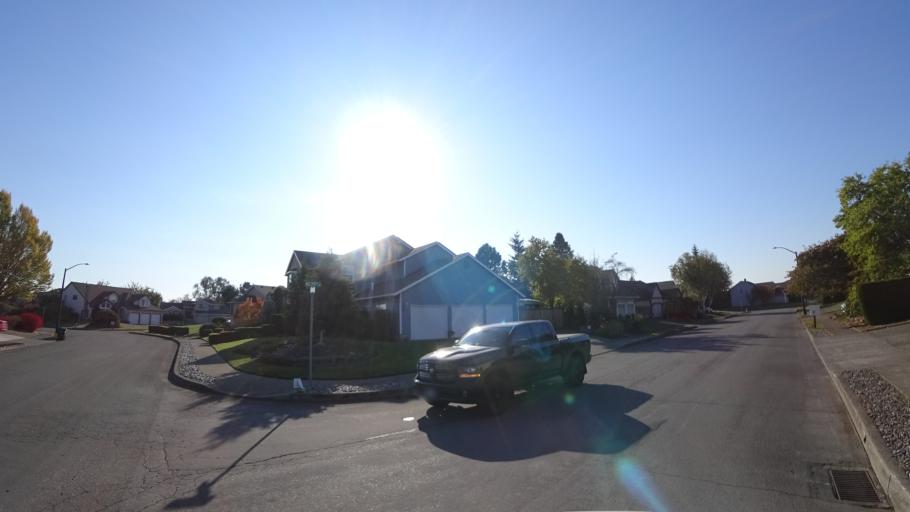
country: US
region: Oregon
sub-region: Multnomah County
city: Wood Village
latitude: 45.5177
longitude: -122.4273
